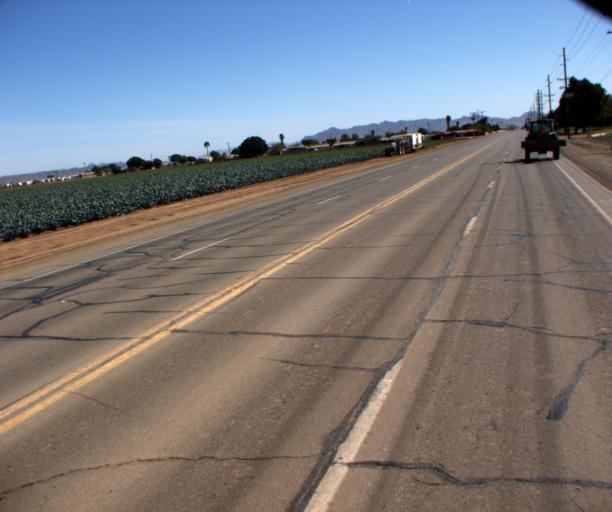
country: US
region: Arizona
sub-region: Yuma County
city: Yuma
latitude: 32.6991
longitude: -114.5337
